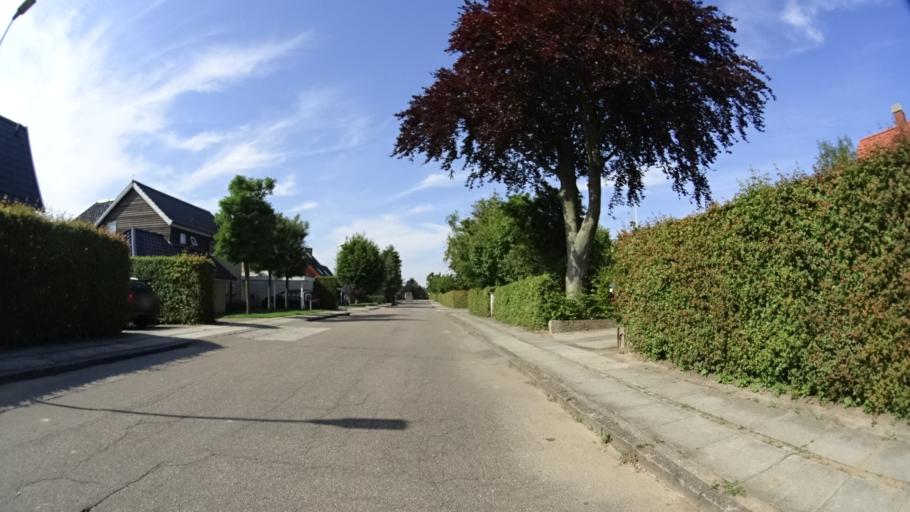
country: DK
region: Central Jutland
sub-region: Arhus Kommune
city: Stavtrup
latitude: 56.1184
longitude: 10.1685
